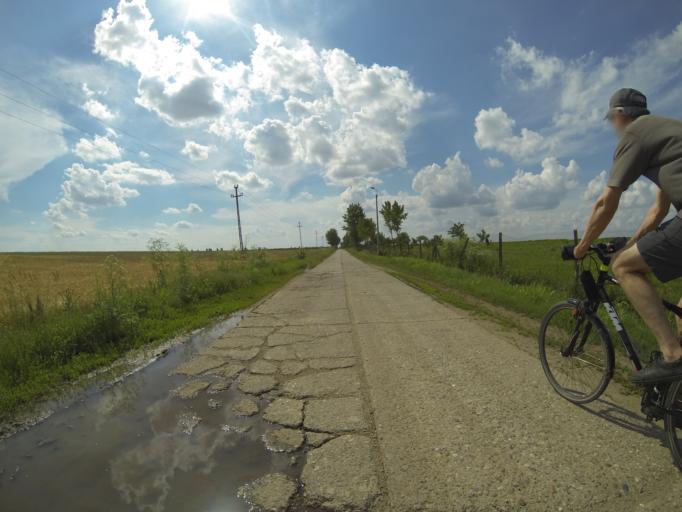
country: RO
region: Dolj
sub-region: Comuna Segarcea
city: Segarcea
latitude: 44.1081
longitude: 23.7344
